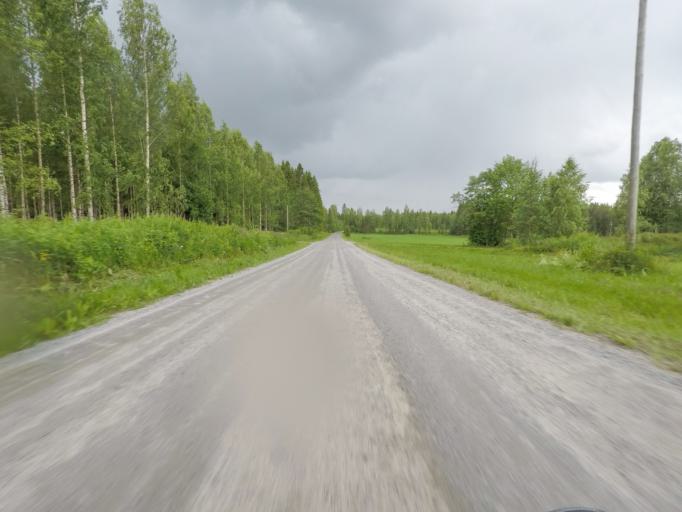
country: FI
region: Central Finland
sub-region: Jyvaeskylae
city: Hankasalmi
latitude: 62.4006
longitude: 26.6020
